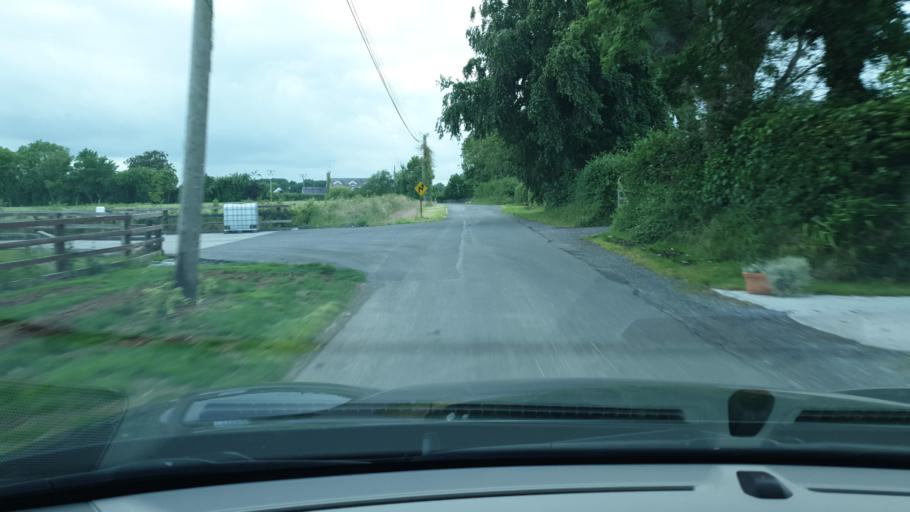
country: IE
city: Kentstown
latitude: 53.5751
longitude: -6.5142
